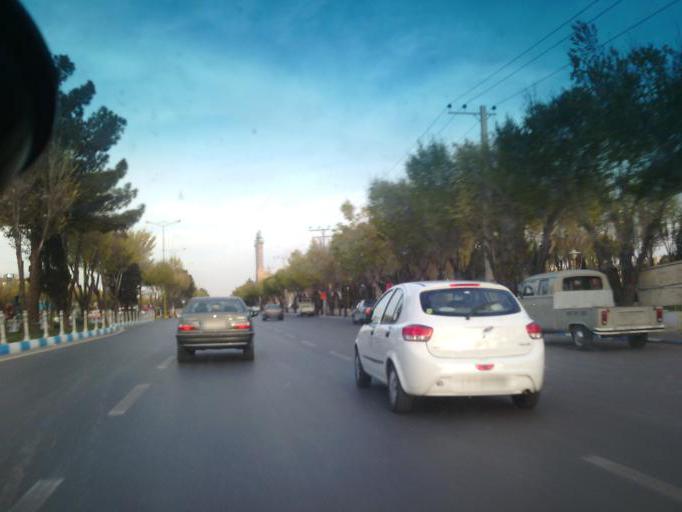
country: IR
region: Isfahan
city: Shahin Shahr
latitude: 32.8614
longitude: 51.5367
